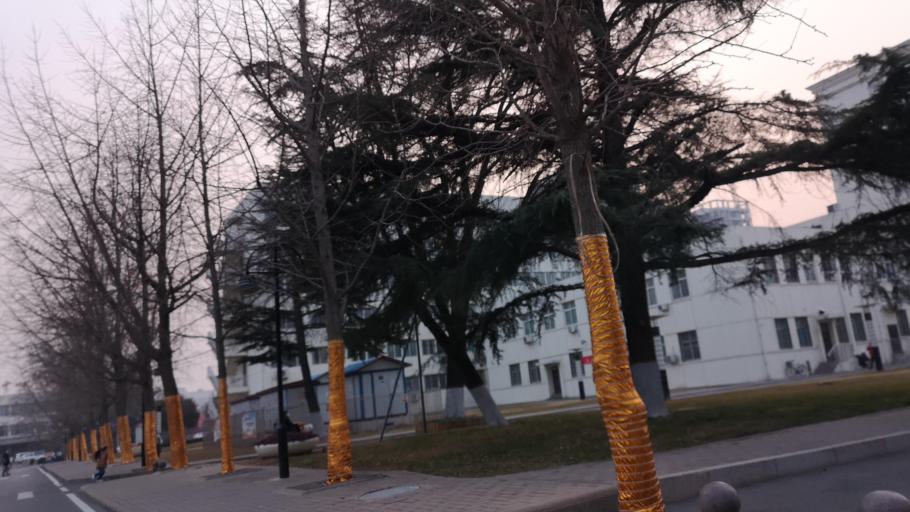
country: CN
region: Henan Sheng
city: Zhongyuanlu
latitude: 35.7771
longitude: 115.0754
